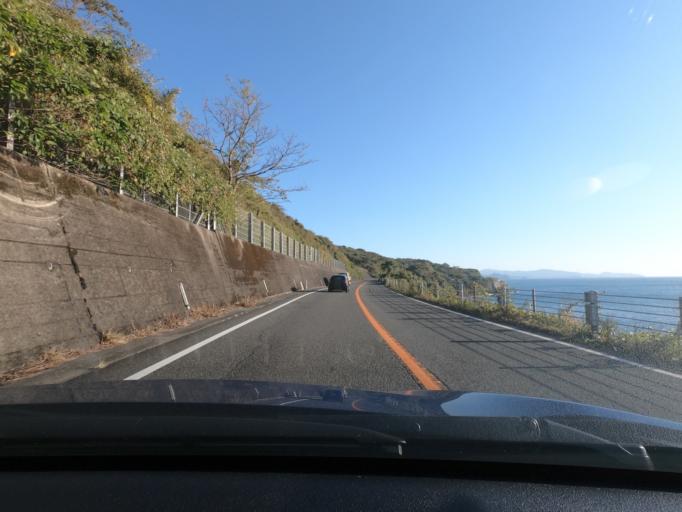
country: JP
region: Kagoshima
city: Akune
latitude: 31.9561
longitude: 130.2155
